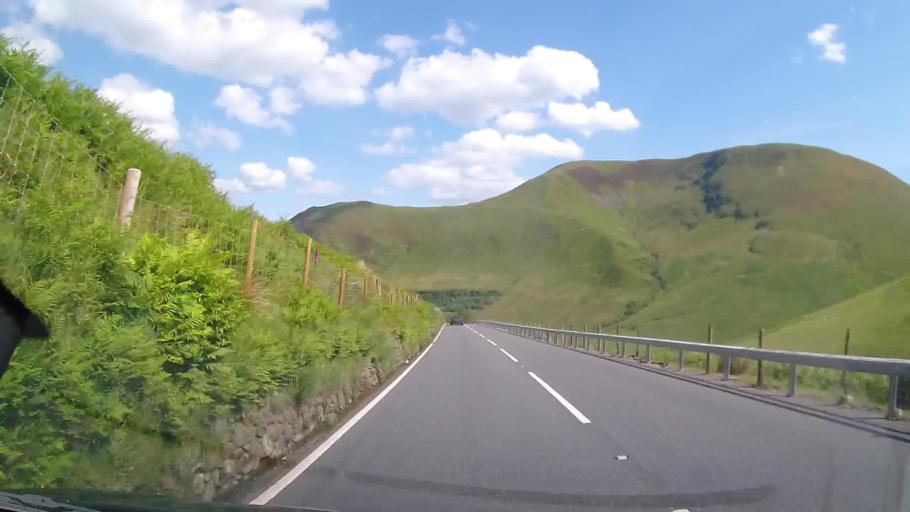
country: GB
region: Wales
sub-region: Gwynedd
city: Corris
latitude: 52.7336
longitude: -3.7622
